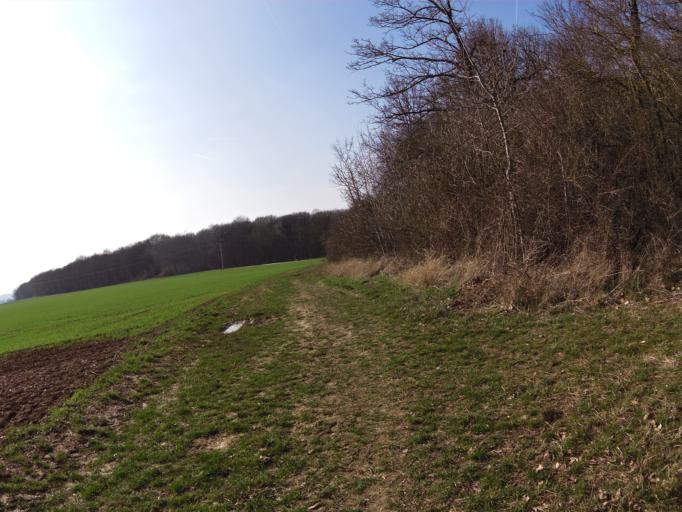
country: DE
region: Bavaria
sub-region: Regierungsbezirk Unterfranken
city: Rottendorf
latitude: 49.8103
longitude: 10.0308
